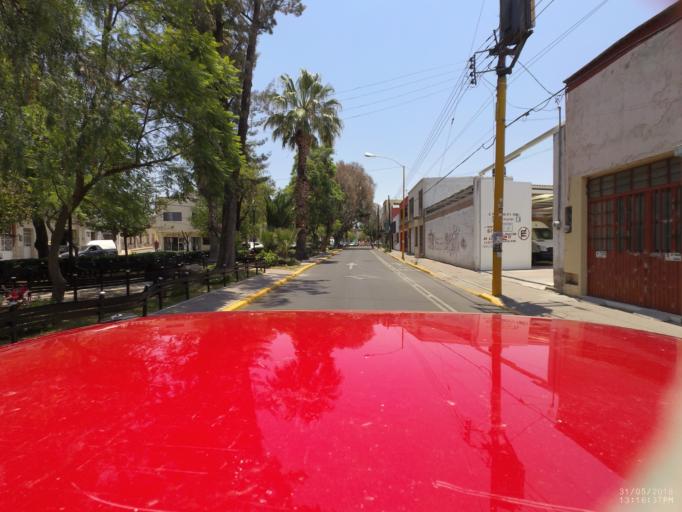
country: MX
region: Aguascalientes
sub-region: Aguascalientes
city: Aguascalientes
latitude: 21.8825
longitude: -102.2864
